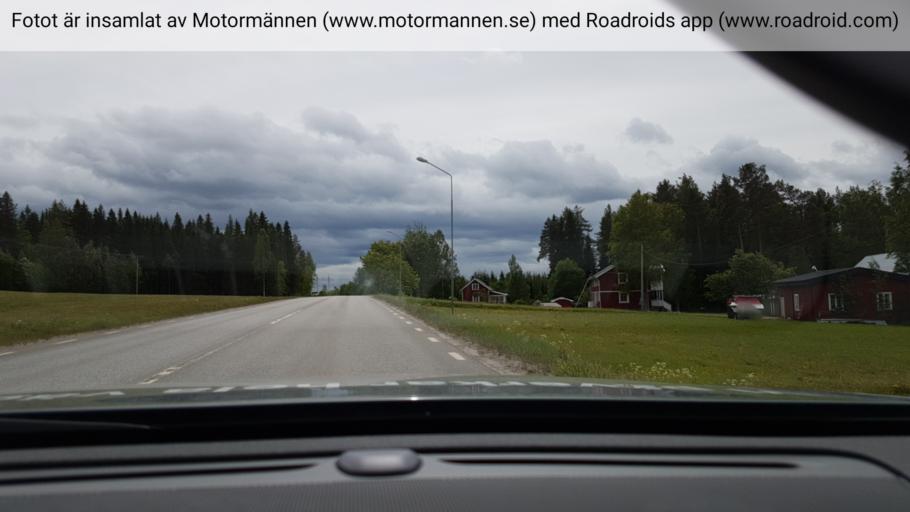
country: SE
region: Vaesterbotten
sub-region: Vannas Kommun
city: Vaennaes
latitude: 63.9808
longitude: 19.7300
